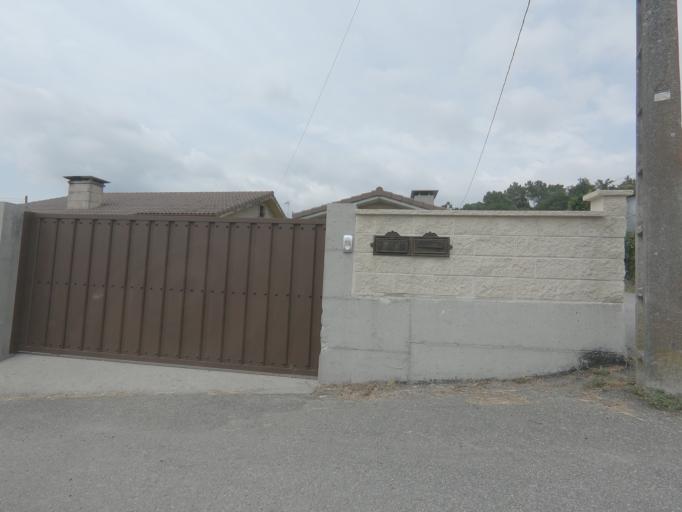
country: ES
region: Galicia
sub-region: Provincia de Pontevedra
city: Ponteareas
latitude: 42.1527
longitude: -8.5002
